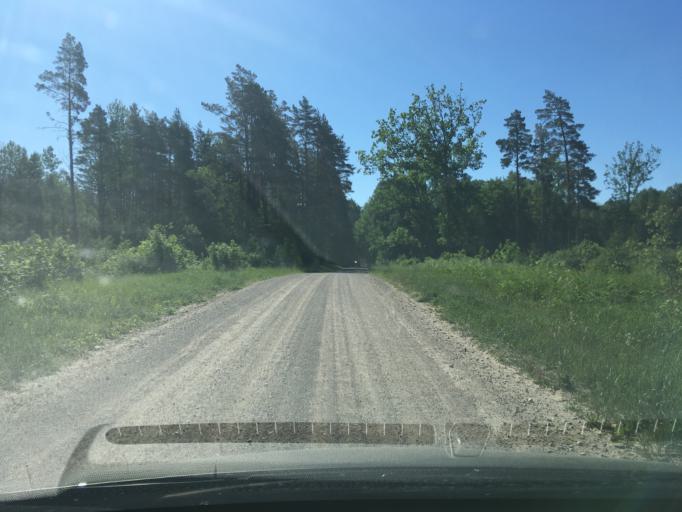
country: EE
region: Laeaene
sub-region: Lihula vald
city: Lihula
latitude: 58.6446
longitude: 23.7854
